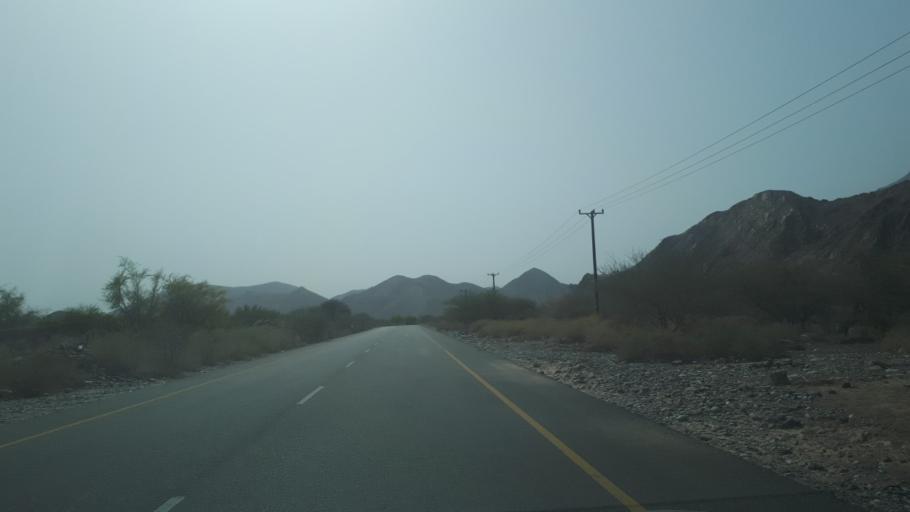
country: OM
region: Muhafazat ad Dakhiliyah
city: Bahla'
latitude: 23.2204
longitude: 57.0011
